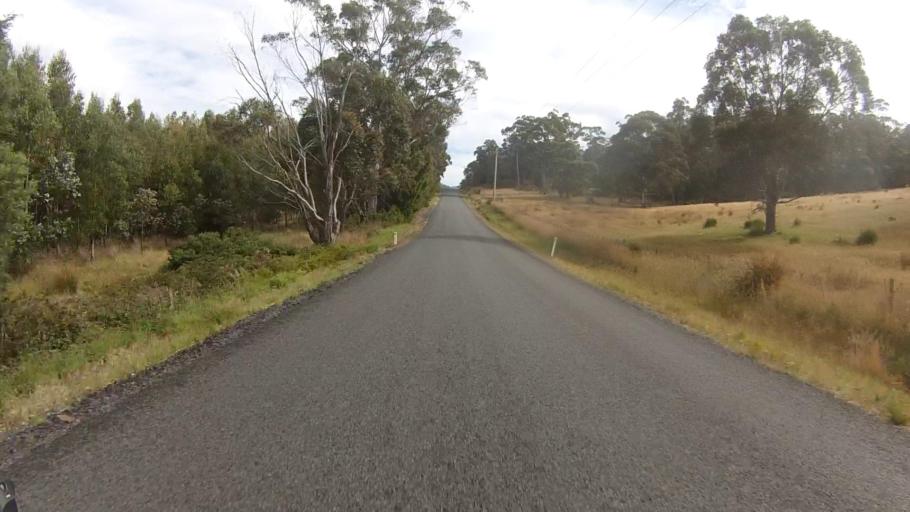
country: AU
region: Tasmania
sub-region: Sorell
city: Sorell
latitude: -42.8036
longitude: 147.7932
